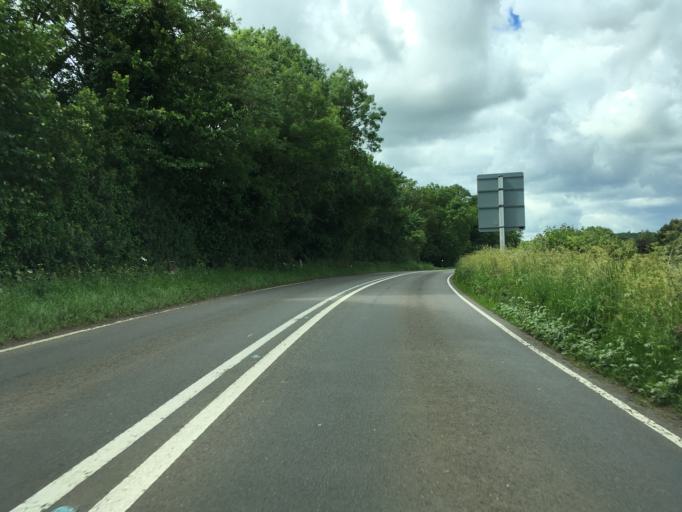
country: GB
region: England
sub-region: Oxfordshire
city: Hook Norton
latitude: 51.9762
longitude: -1.4388
